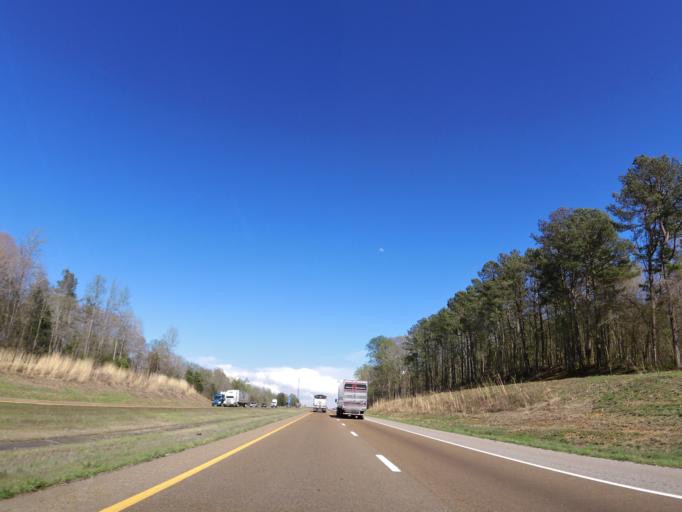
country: US
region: Tennessee
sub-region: Decatur County
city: Parsons
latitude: 35.8182
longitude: -88.1827
